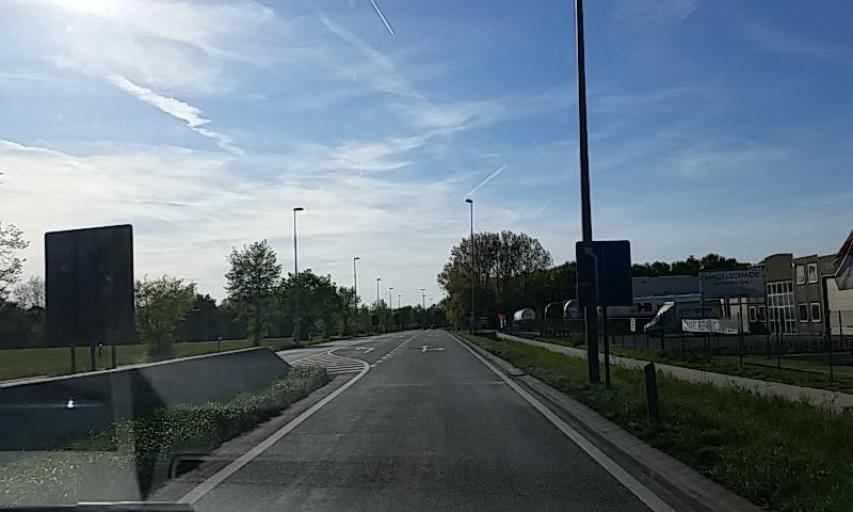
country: BE
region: Flanders
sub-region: Provincie Oost-Vlaanderen
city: Zelzate
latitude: 51.1880
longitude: 3.8296
